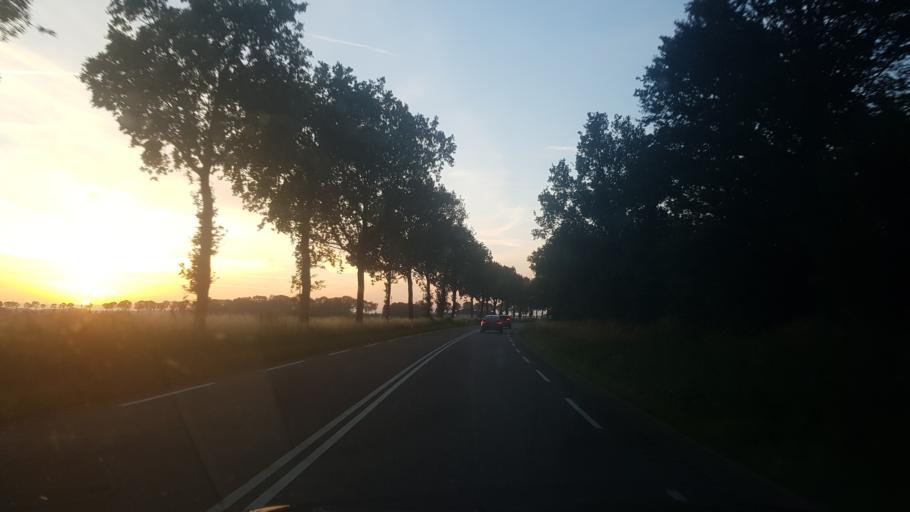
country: NL
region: Flevoland
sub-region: Gemeente Noordoostpolder
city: Emmeloord
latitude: 52.7021
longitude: 5.7207
